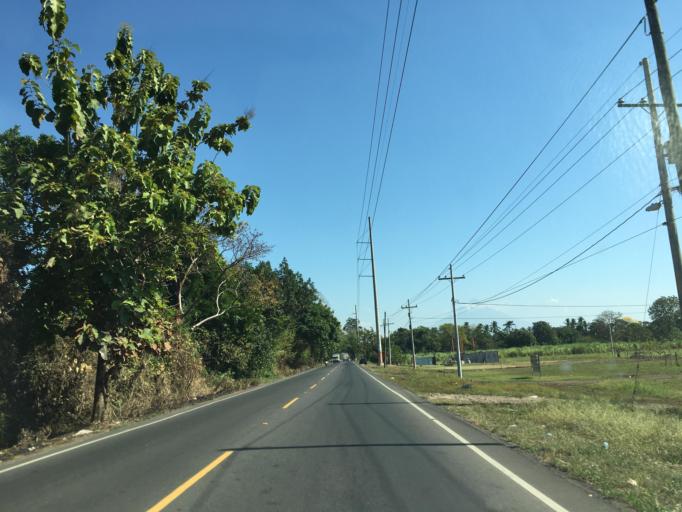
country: GT
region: Escuintla
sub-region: Municipio de La Democracia
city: La Democracia
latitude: 14.2191
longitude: -90.9526
